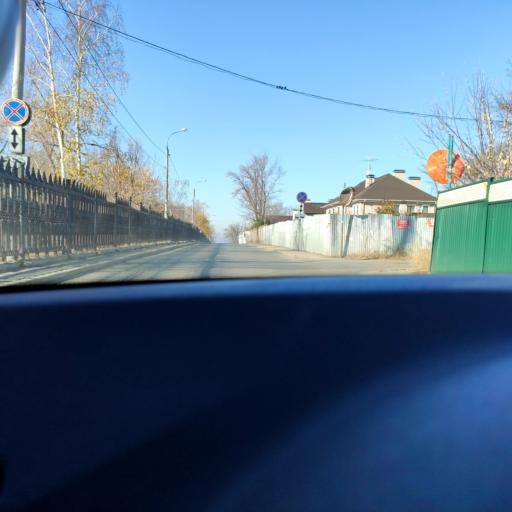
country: RU
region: Samara
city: Samara
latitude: 53.2289
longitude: 50.1729
